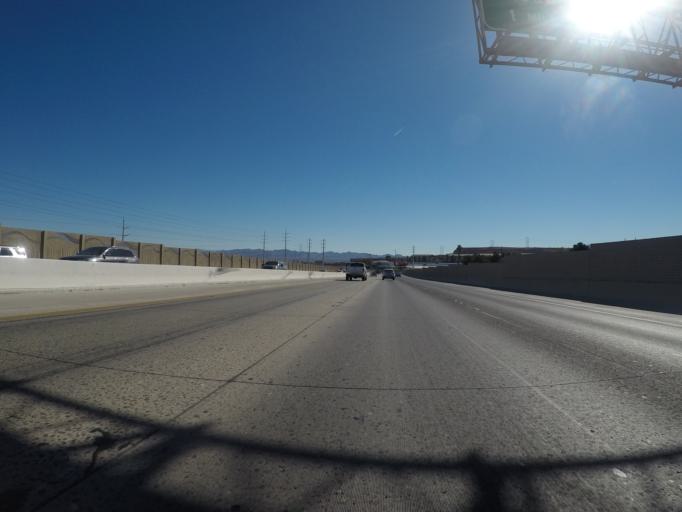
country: US
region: Nevada
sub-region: Clark County
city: Whitney
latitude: 36.0908
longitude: -115.0715
